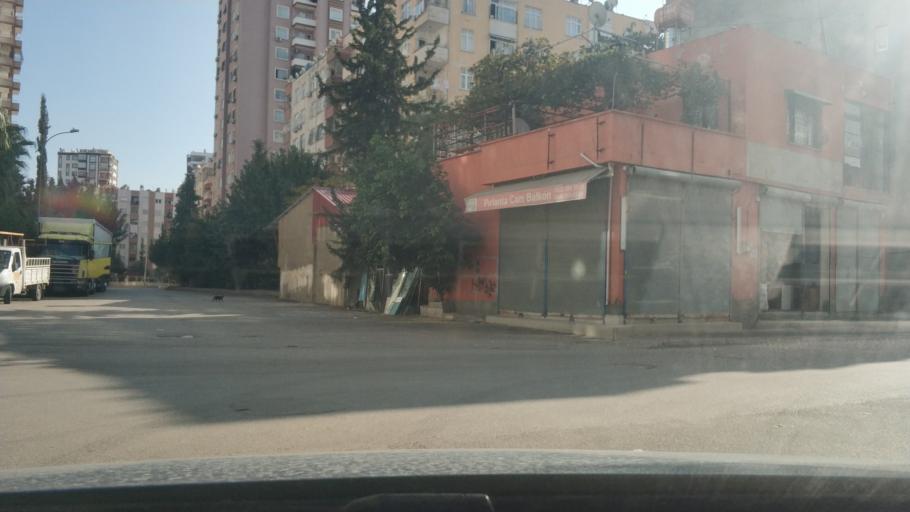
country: TR
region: Adana
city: Seyhan
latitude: 37.0185
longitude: 35.2877
